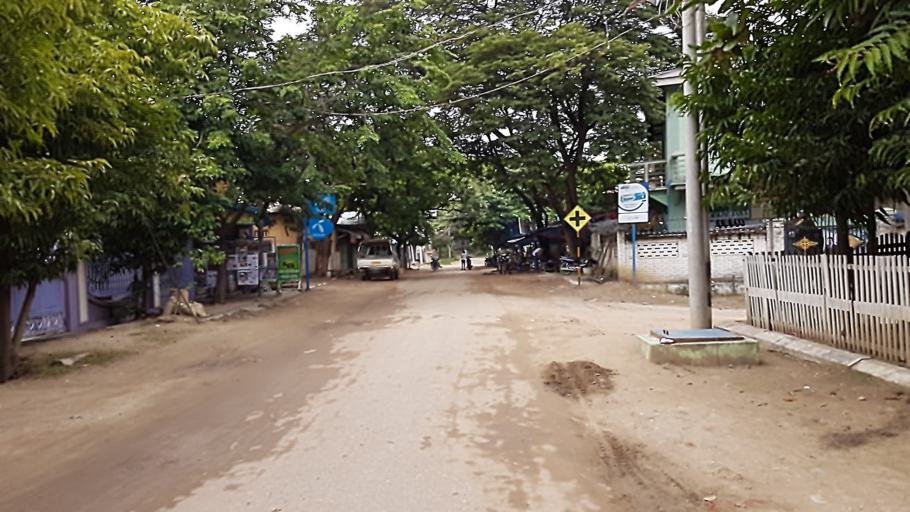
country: MM
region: Magway
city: Minbu
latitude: 20.1734
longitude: 94.8779
